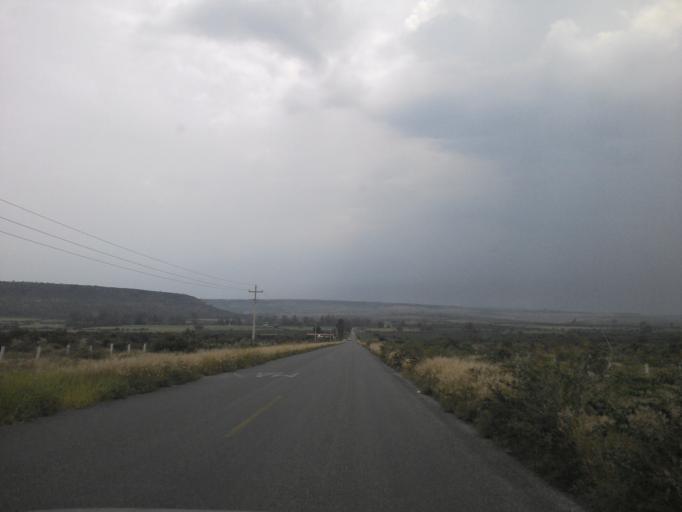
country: MX
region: Jalisco
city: San Diego de Alejandria
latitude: 20.9028
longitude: -102.0488
